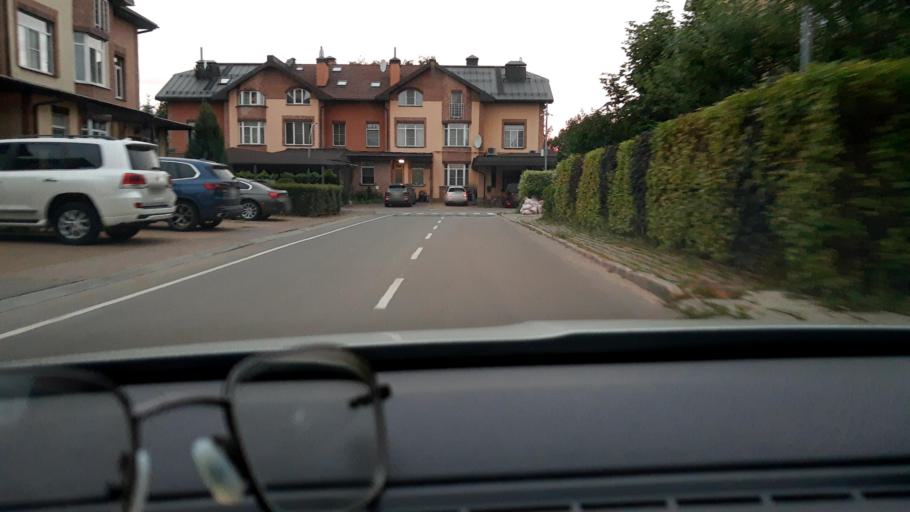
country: RU
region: Moskovskaya
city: Kommunarka
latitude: 55.5705
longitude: 37.4434
